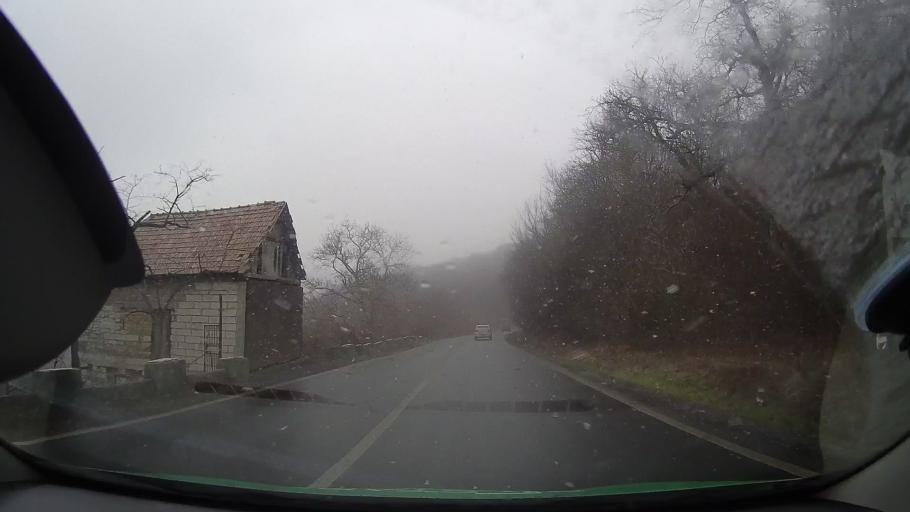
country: RO
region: Sibiu
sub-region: Municipiul Medias
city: Medias
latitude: 46.1792
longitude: 24.3402
